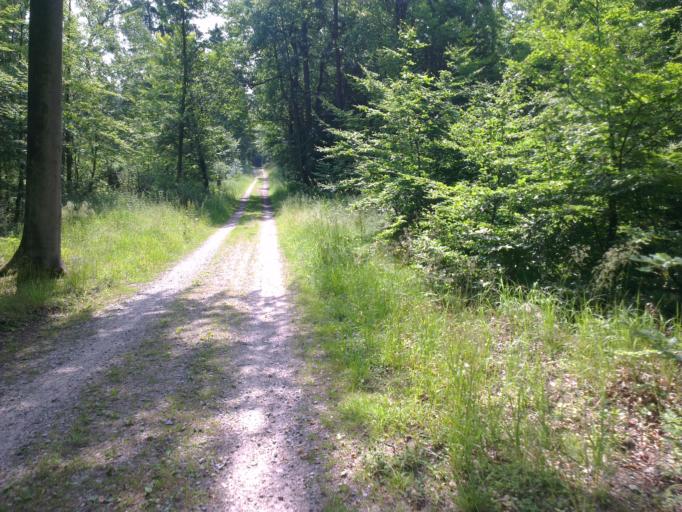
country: DK
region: Capital Region
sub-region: Allerod Kommune
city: Lillerod
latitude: 55.9039
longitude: 12.3696
